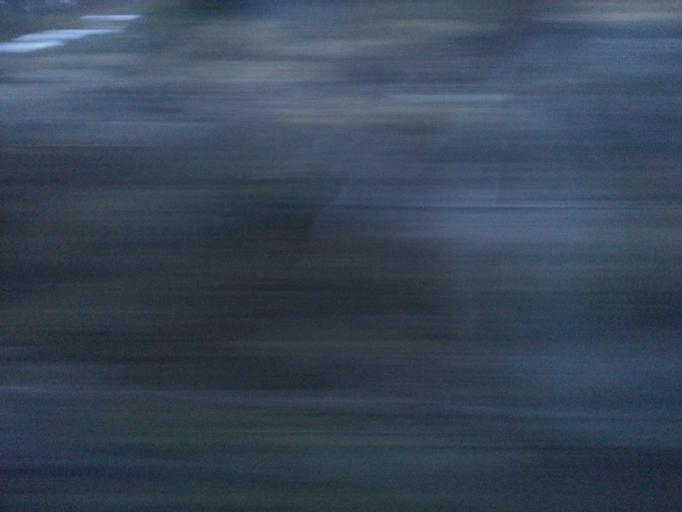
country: NO
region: Sor-Trondelag
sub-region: Rennebu
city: Berkak
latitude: 62.6974
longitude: 9.9456
